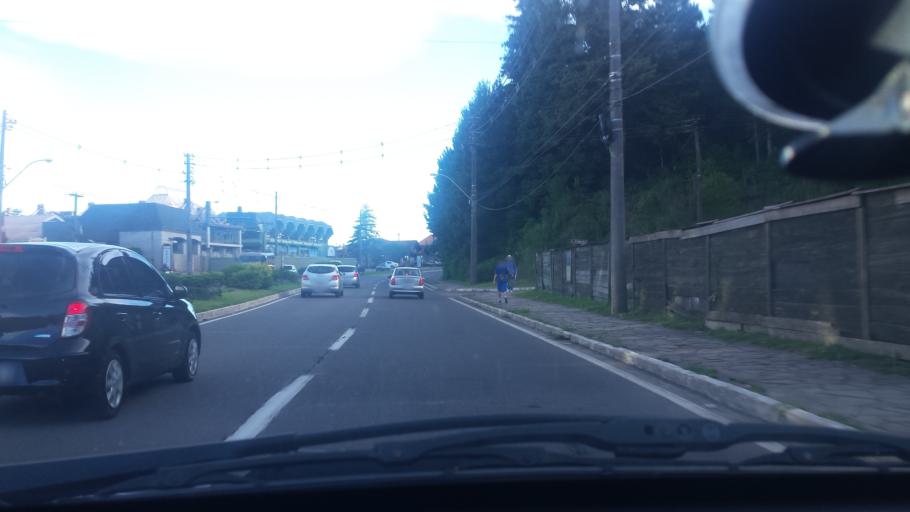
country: BR
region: Rio Grande do Sul
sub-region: Canela
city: Canela
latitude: -29.3750
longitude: -50.8648
